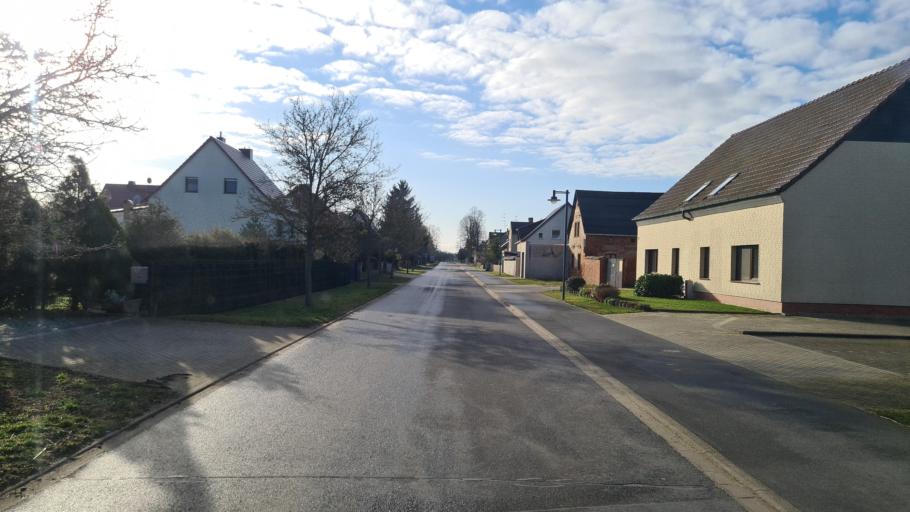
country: DE
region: Brandenburg
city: Herzberg
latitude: 51.7005
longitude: 13.2171
